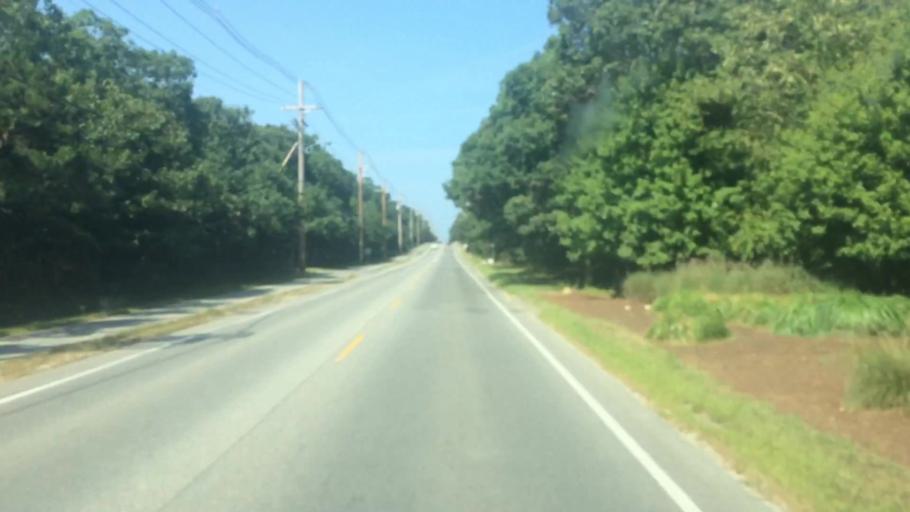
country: US
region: Massachusetts
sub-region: Dukes County
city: Vineyard Haven
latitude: 41.4162
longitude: -70.5847
